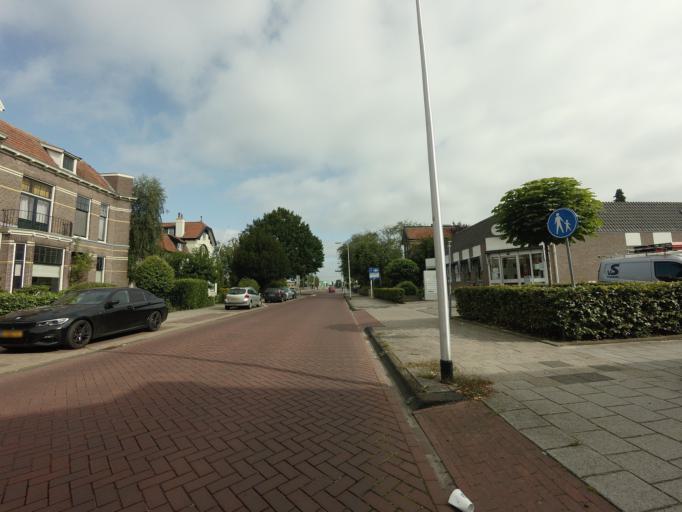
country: NL
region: Overijssel
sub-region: Gemeente Steenwijkerland
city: Steenwijk
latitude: 52.7892
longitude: 6.1209
